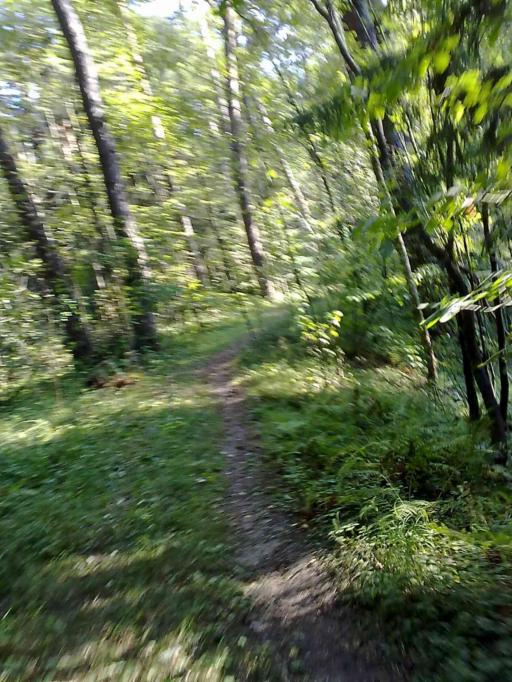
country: RU
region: Moskovskaya
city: Gorki Vtoryye
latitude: 55.6739
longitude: 37.1608
